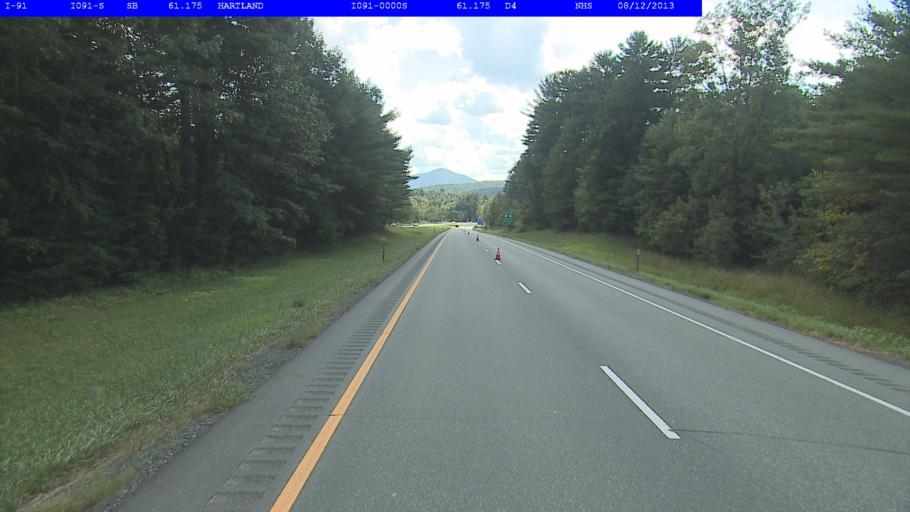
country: US
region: Vermont
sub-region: Windsor County
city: Windsor
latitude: 43.5355
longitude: -72.3928
